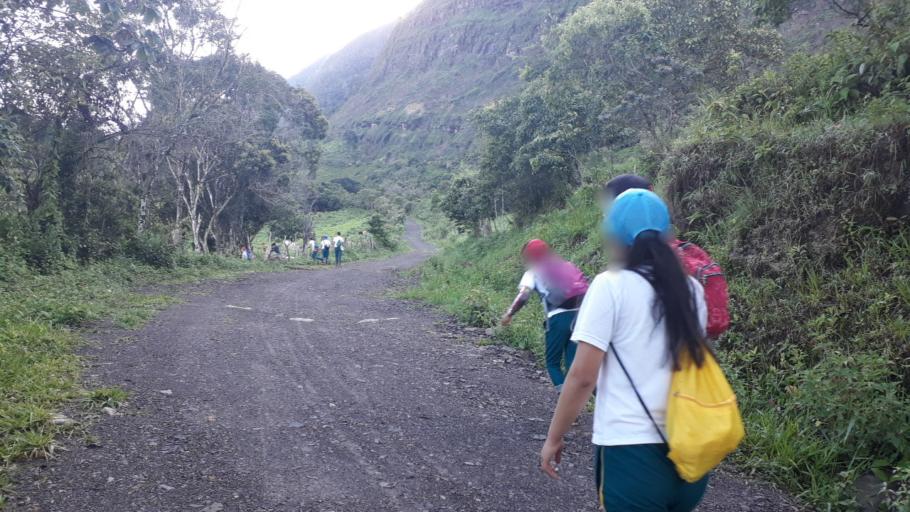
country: CO
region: Casanare
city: Nunchia
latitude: 5.6560
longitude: -72.4228
